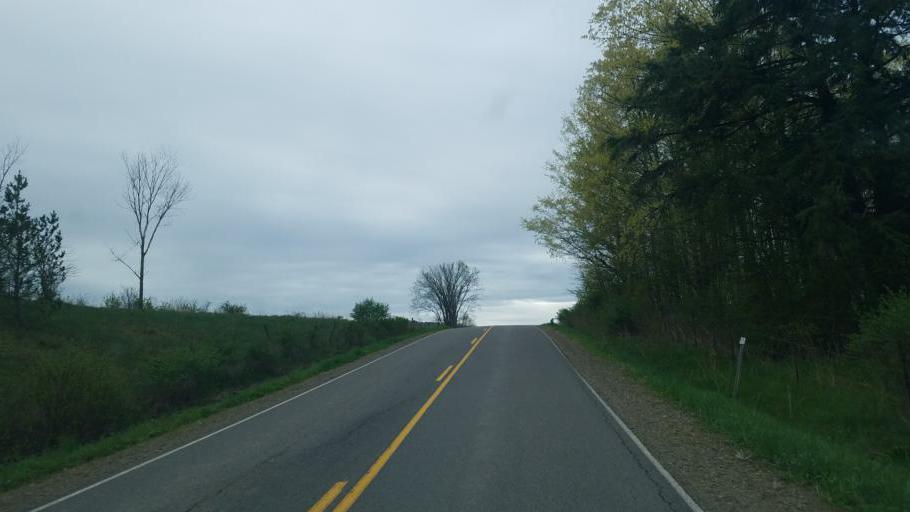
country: US
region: Pennsylvania
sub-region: Tioga County
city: Westfield
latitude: 42.0302
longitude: -77.4663
